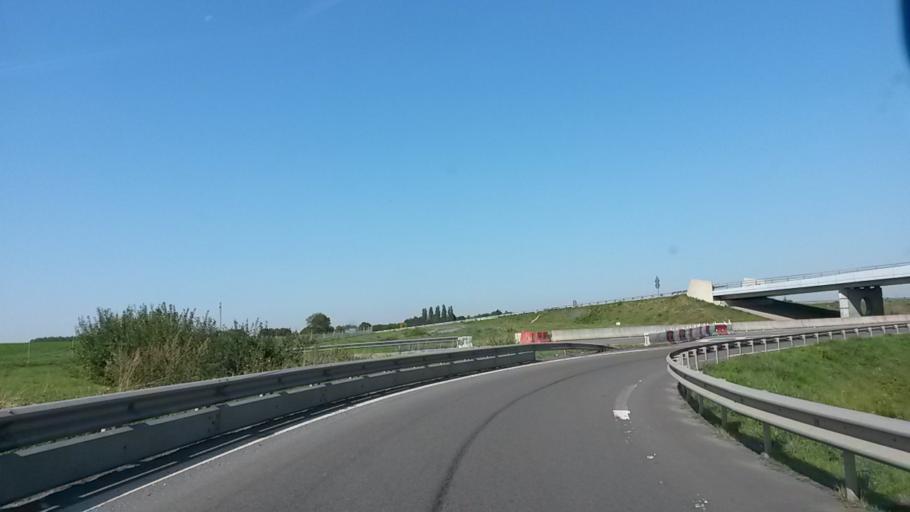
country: FR
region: Nord-Pas-de-Calais
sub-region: Departement du Nord
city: Hautmont
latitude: 50.2064
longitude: 3.9560
